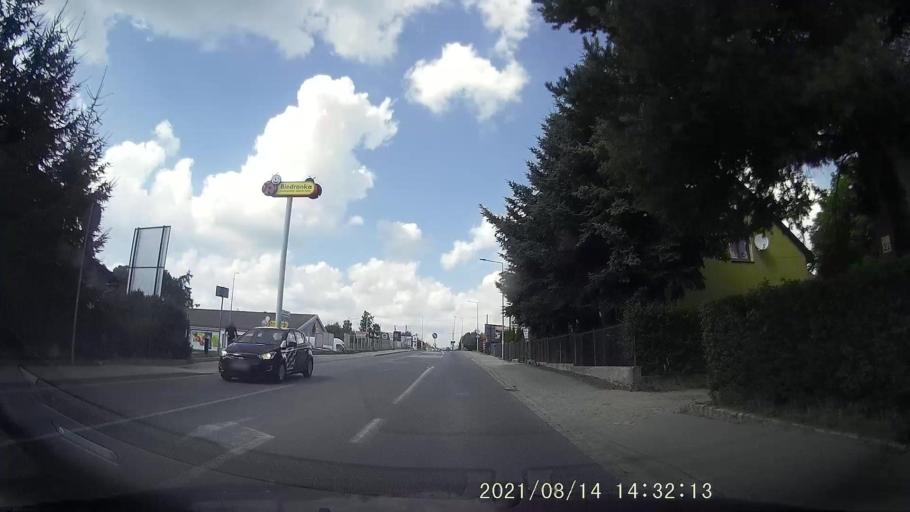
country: PL
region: Lower Silesian Voivodeship
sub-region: Powiat klodzki
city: Bozkow
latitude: 50.5482
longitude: 16.5507
